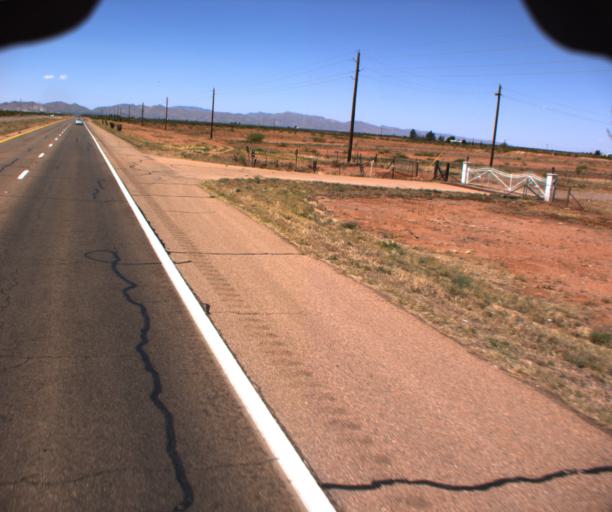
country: US
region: Arizona
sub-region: Cochise County
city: Pirtleville
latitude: 31.3567
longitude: -109.6256
